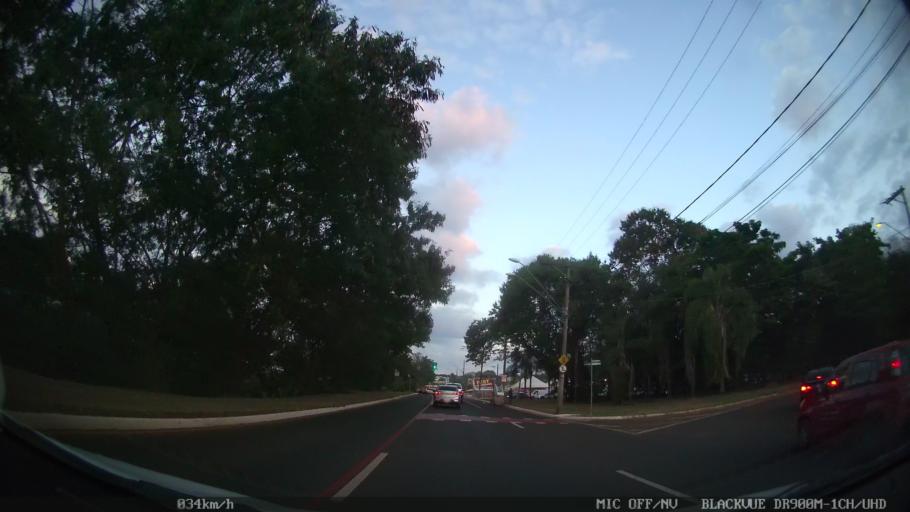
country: BR
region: Sao Paulo
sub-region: Ribeirao Preto
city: Ribeirao Preto
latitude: -21.2067
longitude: -47.7914
